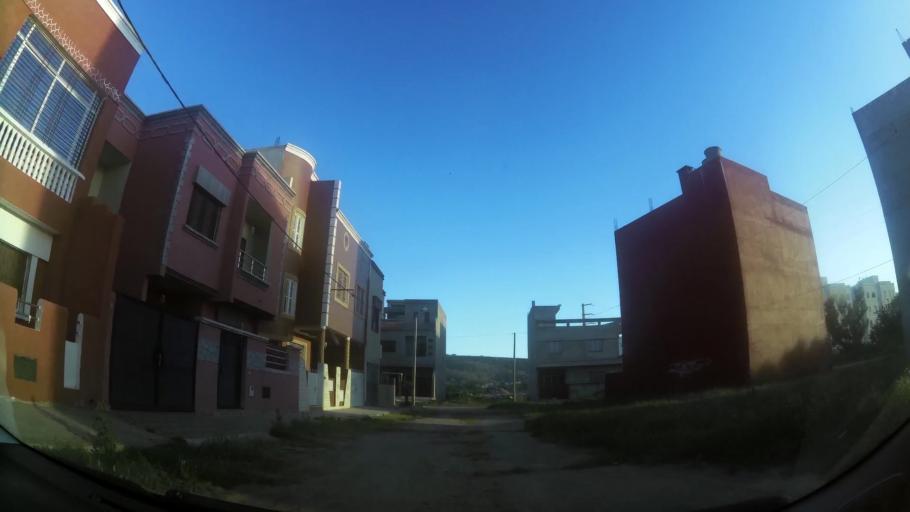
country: MA
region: Oriental
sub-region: Berkane-Taourirt
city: Madagh
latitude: 35.0772
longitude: -2.2345
